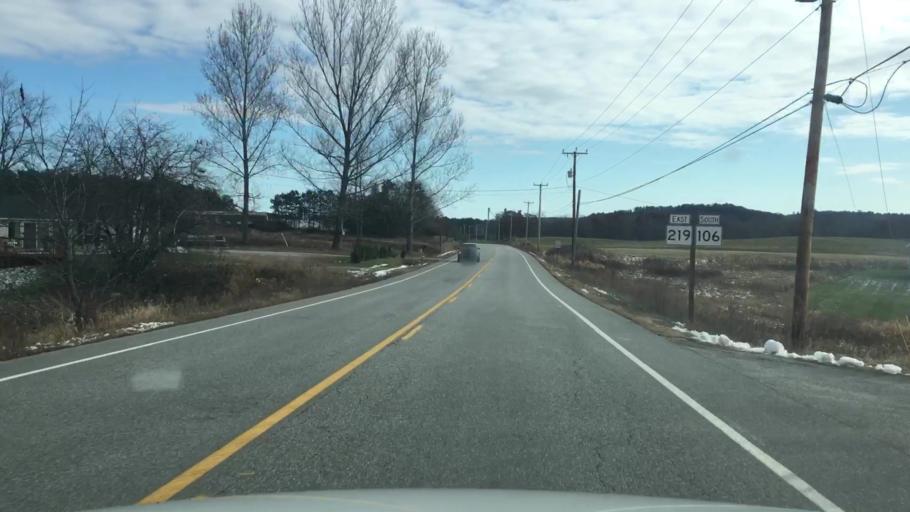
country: US
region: Maine
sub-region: Androscoggin County
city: Leeds
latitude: 44.3449
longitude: -70.1447
